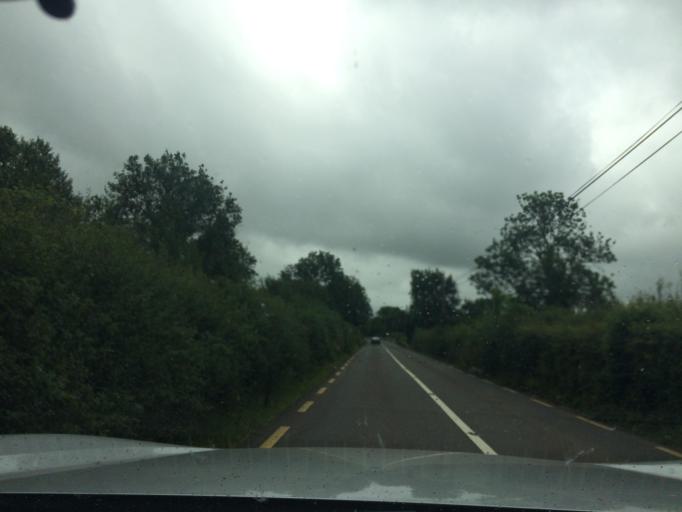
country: IE
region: Munster
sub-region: South Tipperary
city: Cluain Meala
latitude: 52.3133
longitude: -7.7856
